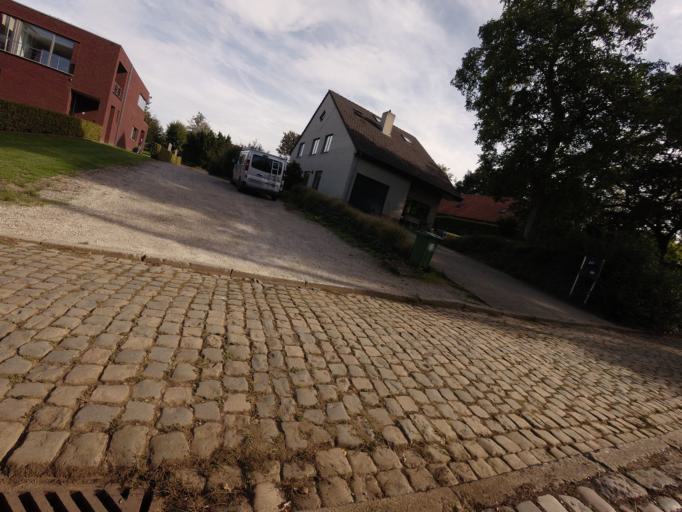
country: BE
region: Flanders
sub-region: Provincie Vlaams-Brabant
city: Herent
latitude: 50.8977
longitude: 4.6726
